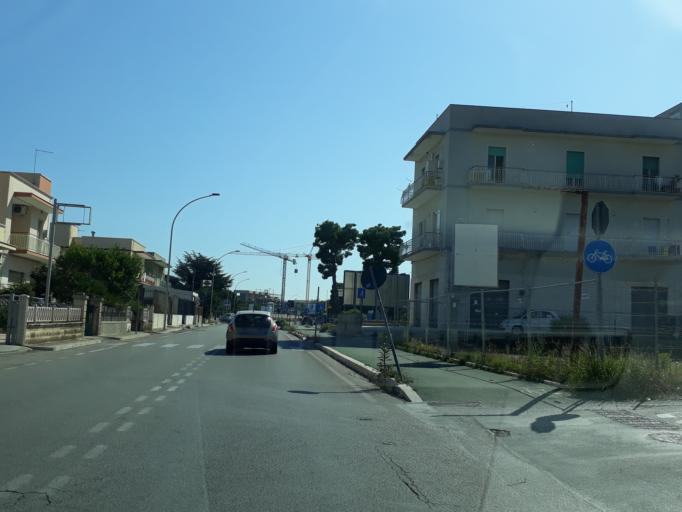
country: IT
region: Apulia
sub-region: Provincia di Bari
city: Monopoli
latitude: 40.9406
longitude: 17.3060
